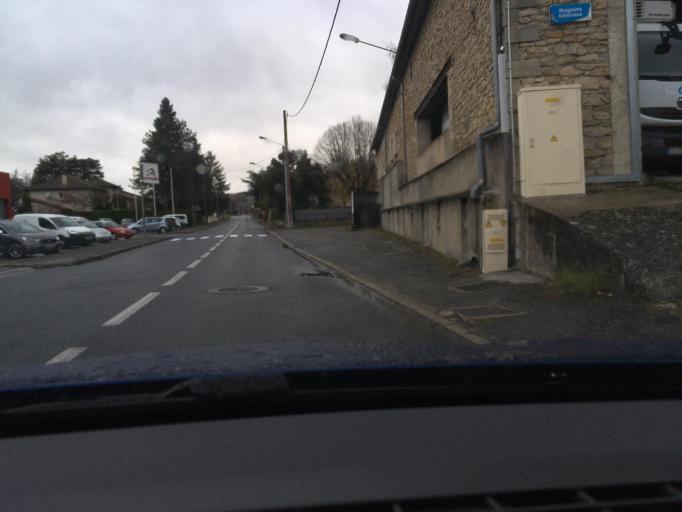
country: FR
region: Midi-Pyrenees
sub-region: Departement de l'Aveyron
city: Villefranche-de-Rouergue
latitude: 44.3593
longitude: 2.0265
